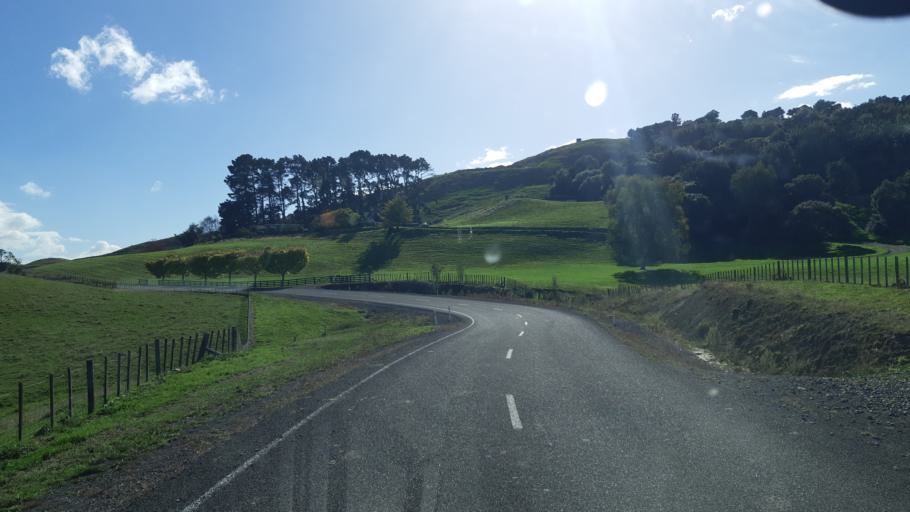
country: NZ
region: Manawatu-Wanganui
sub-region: Rangitikei District
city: Bulls
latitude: -39.9038
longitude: 175.3525
